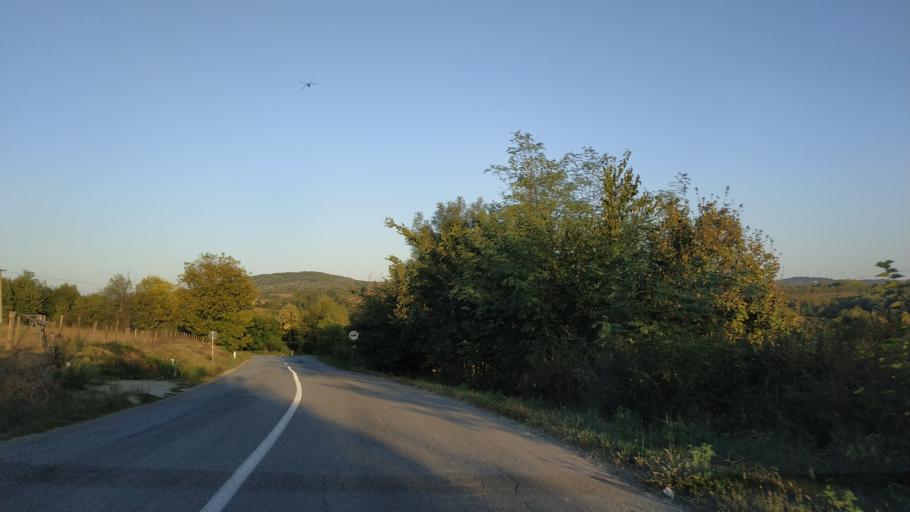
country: RS
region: Central Serbia
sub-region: Sumadijski Okrug
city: Raca
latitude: 44.2411
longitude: 20.8759
